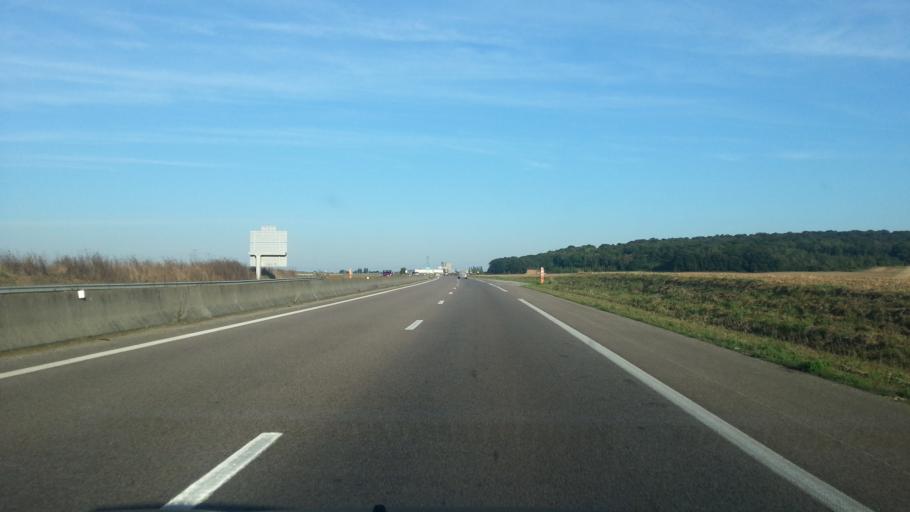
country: FR
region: Picardie
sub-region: Departement de l'Oise
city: Bailleul-sur-Therain
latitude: 49.4119
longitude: 2.2030
